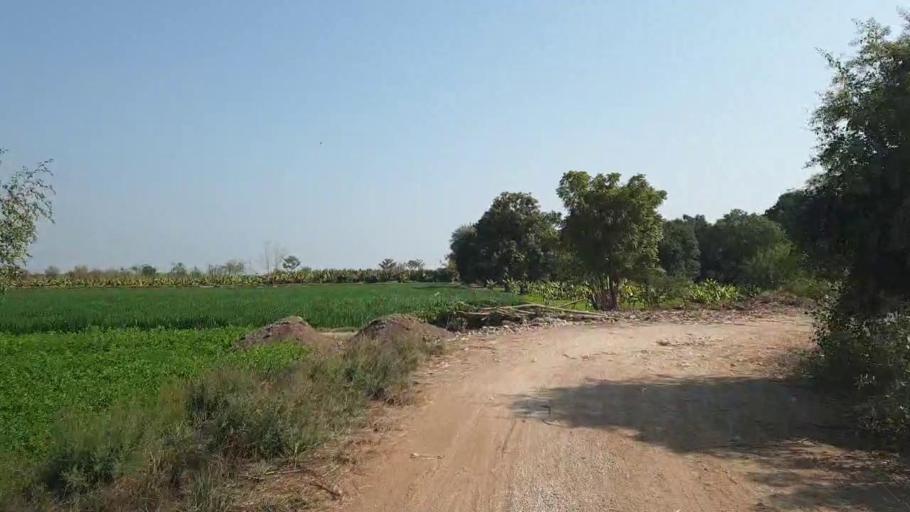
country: PK
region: Sindh
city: Shahdadpur
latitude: 25.9429
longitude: 68.4868
